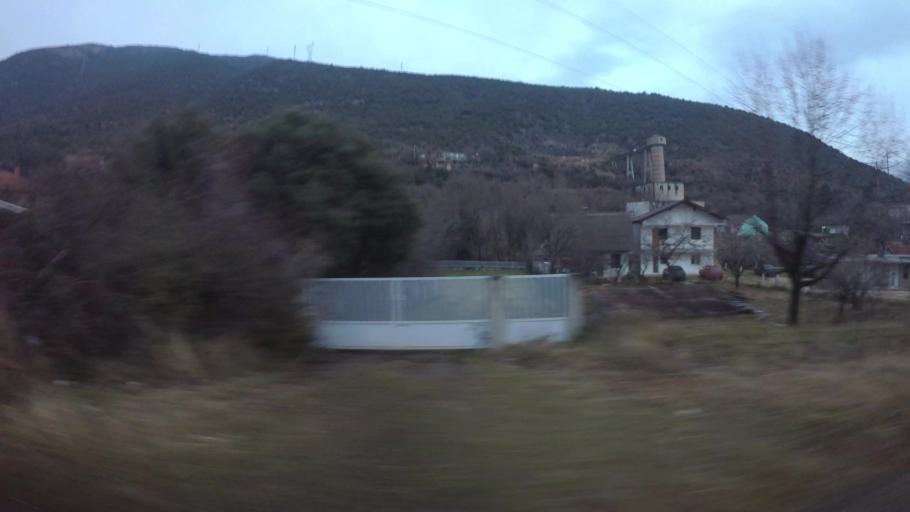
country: BA
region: Federation of Bosnia and Herzegovina
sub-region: Hercegovacko-Bosanski Kanton
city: Mostar
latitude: 43.3681
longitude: 17.8112
